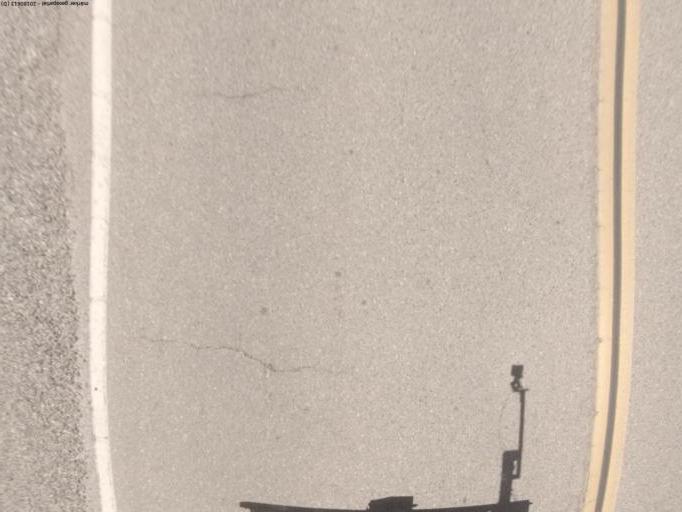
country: US
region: California
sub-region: Madera County
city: Chowchilla
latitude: 37.0472
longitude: -120.3283
